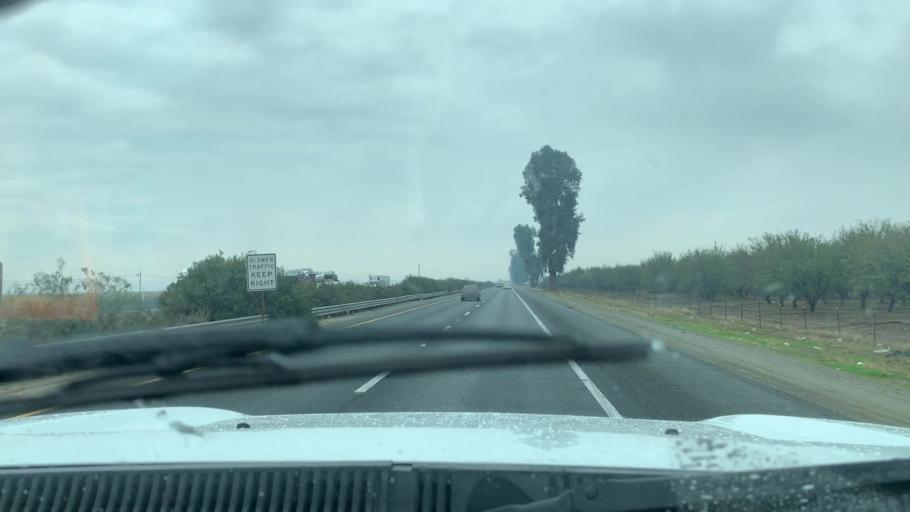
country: US
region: California
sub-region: Kern County
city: Delano
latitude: 35.8002
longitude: -119.2546
